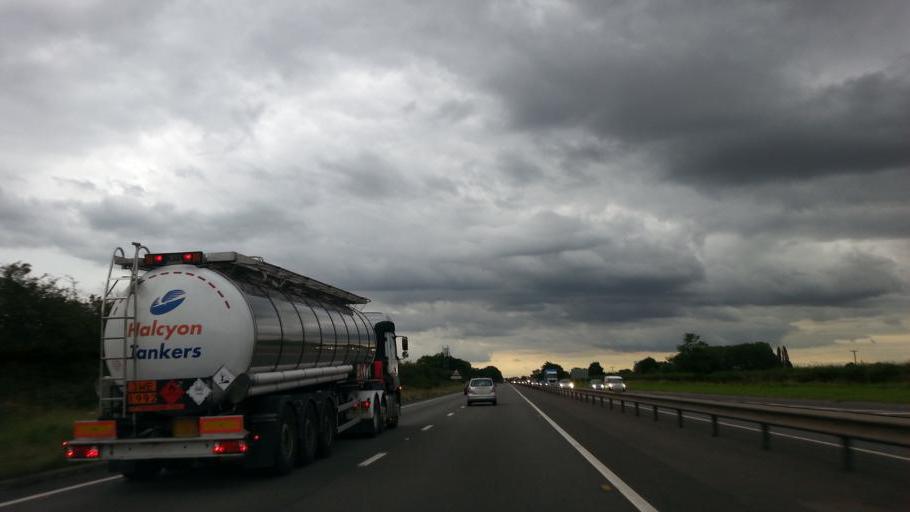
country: GB
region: England
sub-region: Nottinghamshire
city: South Collingham
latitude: 53.1679
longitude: -0.8107
